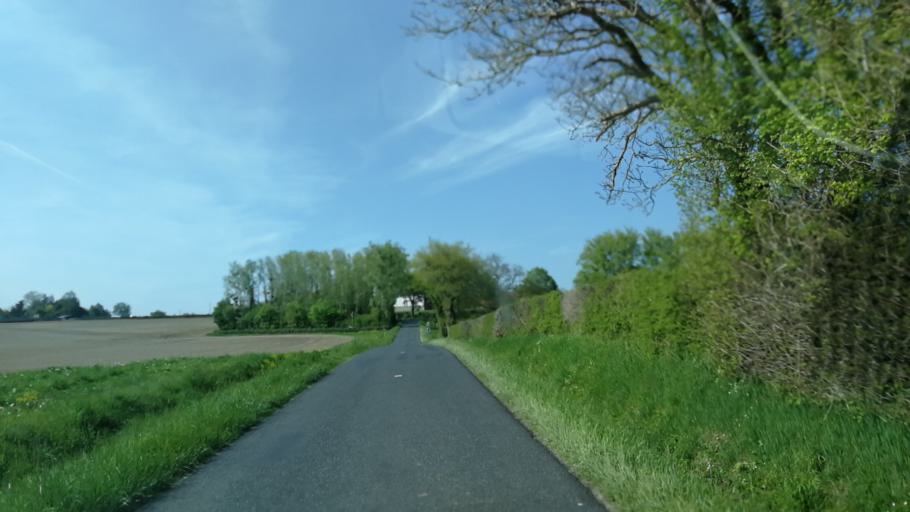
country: FR
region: Auvergne
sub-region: Departement de l'Allier
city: Saint-Gerand-le-Puy
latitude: 46.4018
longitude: 3.5808
